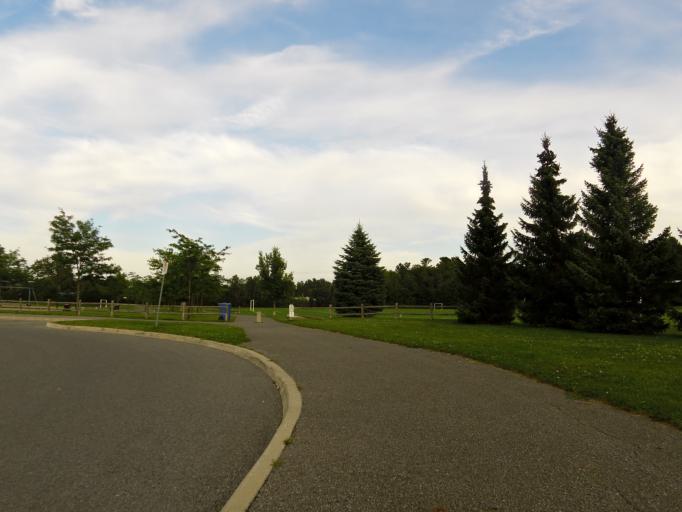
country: CA
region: Ontario
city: Bells Corners
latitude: 45.3254
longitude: -75.7715
